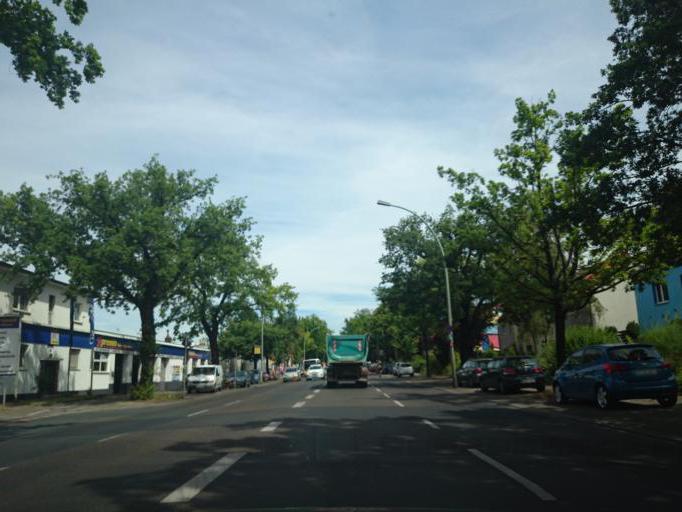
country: DE
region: Berlin
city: Mariendorf
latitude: 52.4324
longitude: 13.3771
